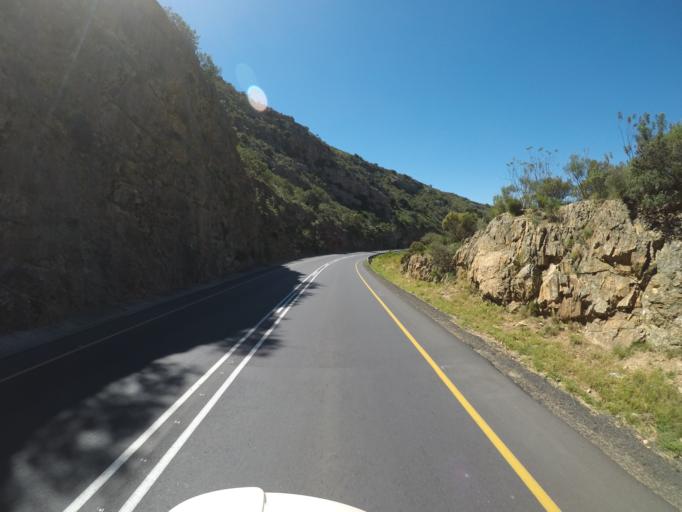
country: ZA
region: Western Cape
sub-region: Cape Winelands District Municipality
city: Ceres
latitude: -33.3176
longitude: 19.0843
